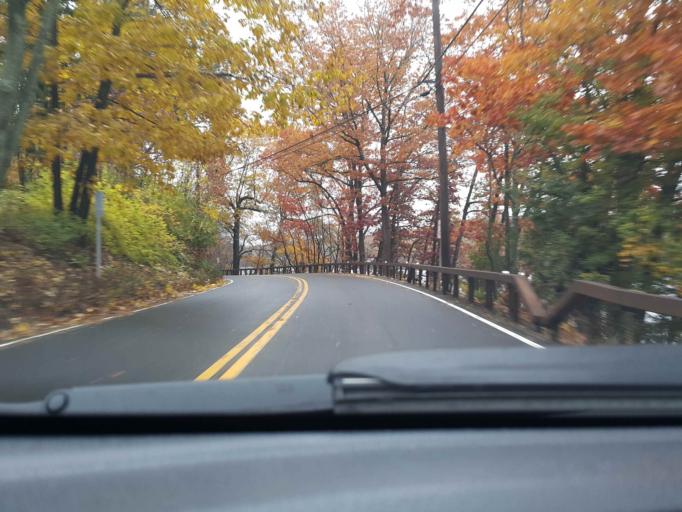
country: US
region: Connecticut
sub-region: New Haven County
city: North Branford
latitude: 41.3852
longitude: -72.7010
